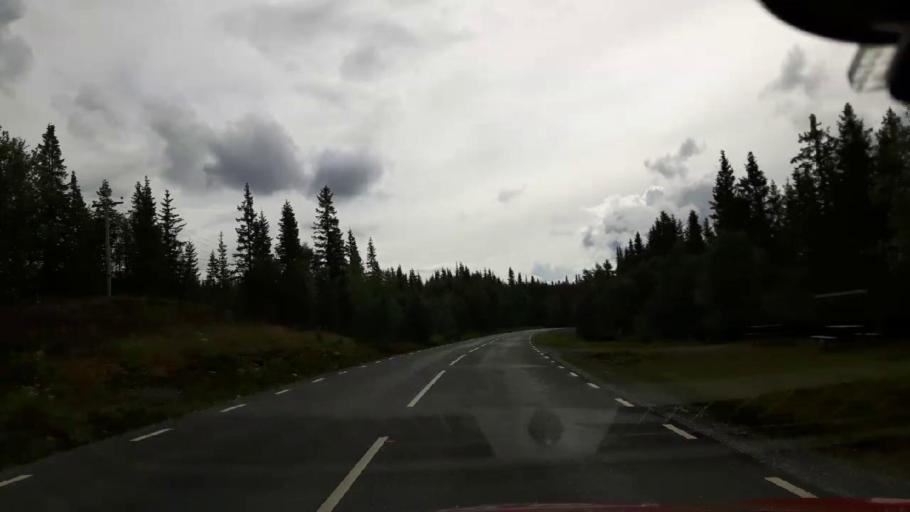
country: NO
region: Nord-Trondelag
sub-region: Lierne
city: Sandvika
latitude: 64.6451
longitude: 14.1423
